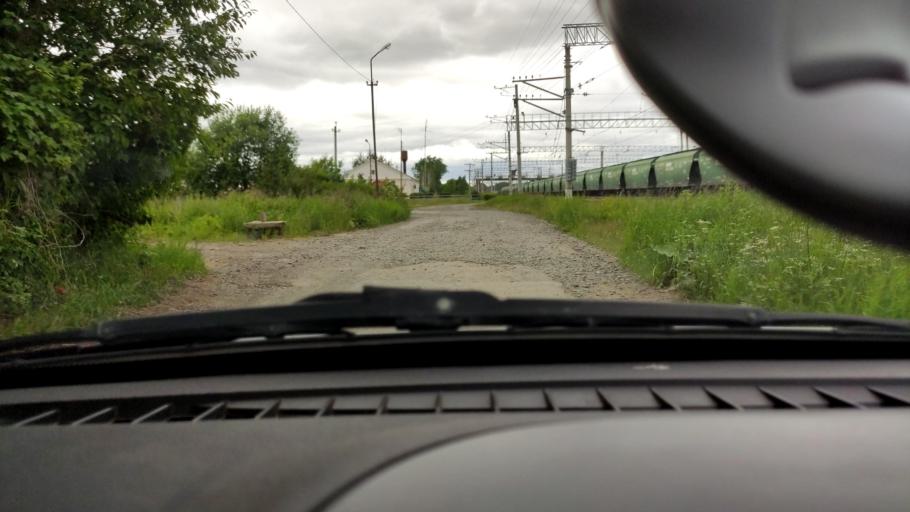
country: RU
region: Perm
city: Ferma
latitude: 57.8922
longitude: 56.2989
